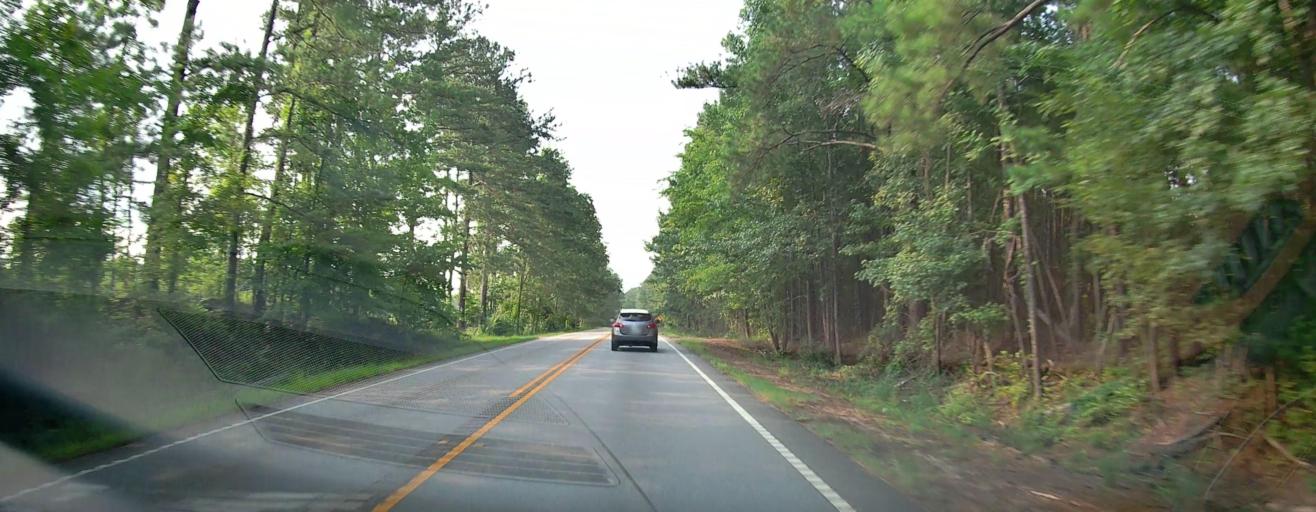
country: US
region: Georgia
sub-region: Monroe County
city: Forsyth
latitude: 33.0272
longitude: -83.7457
